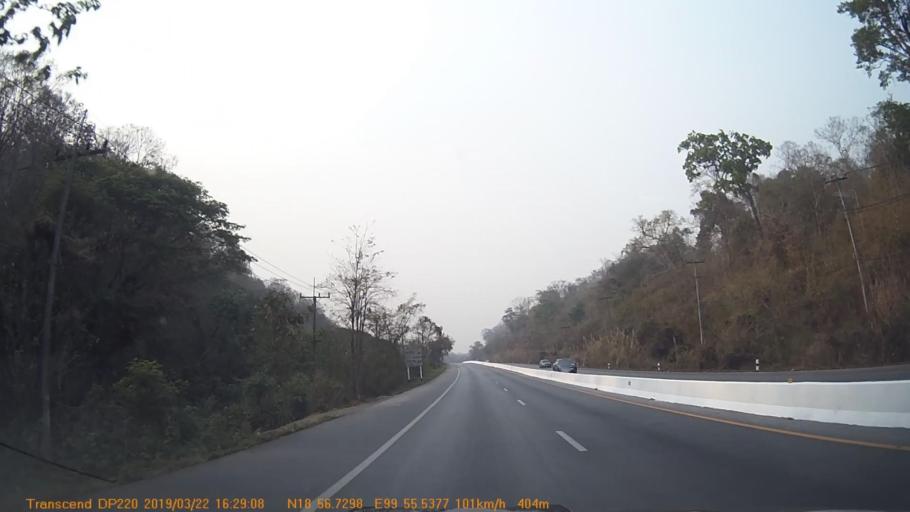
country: TH
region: Lampang
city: Ngao
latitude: 18.9458
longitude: 99.9255
